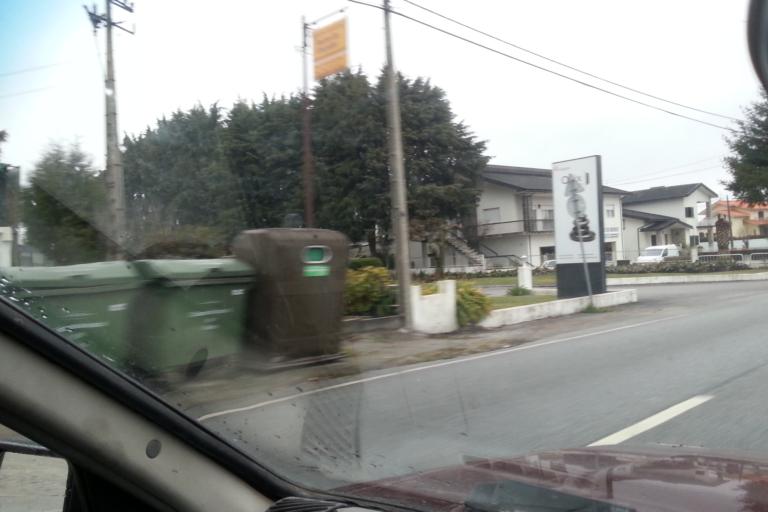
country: PT
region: Viseu
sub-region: Viseu
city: Rio de Loba
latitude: 40.6437
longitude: -7.8650
